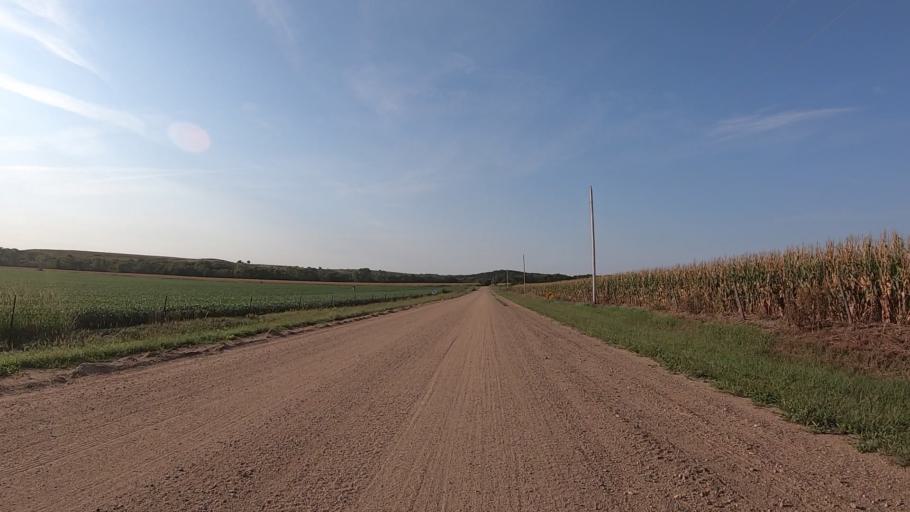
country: US
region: Kansas
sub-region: Marshall County
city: Blue Rapids
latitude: 39.6702
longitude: -96.8062
